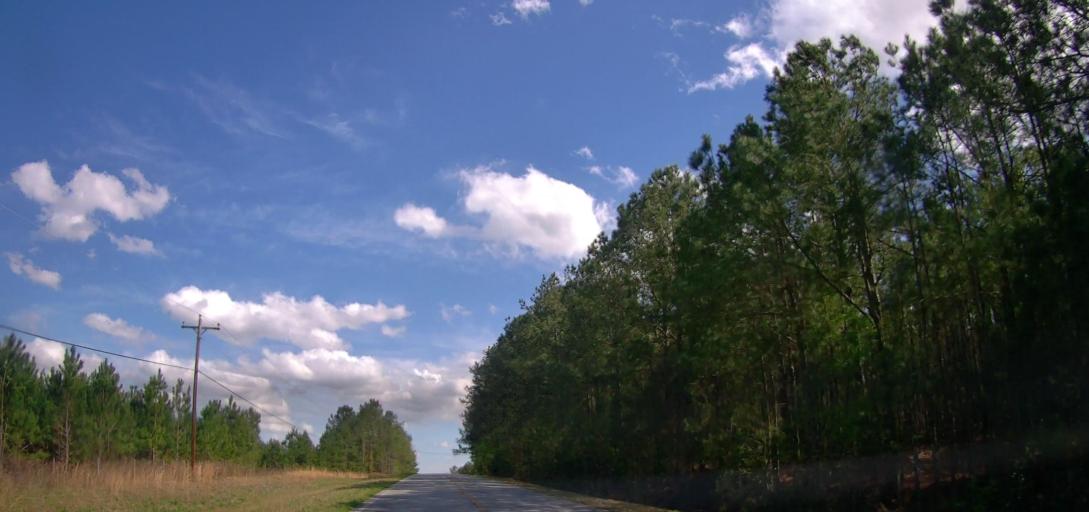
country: US
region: Georgia
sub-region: Wilkinson County
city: Gordon
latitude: 32.8375
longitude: -83.4369
